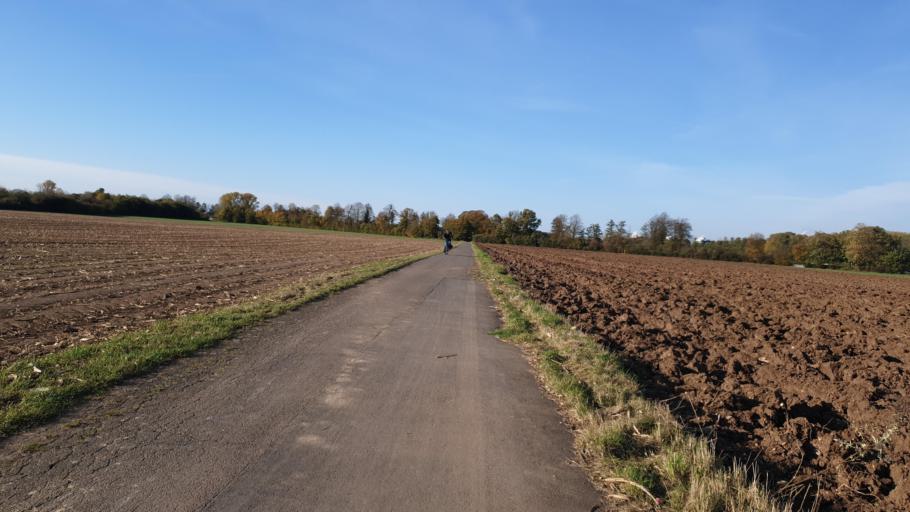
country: DE
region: North Rhine-Westphalia
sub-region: Regierungsbezirk Koln
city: Kerpen
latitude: 50.9208
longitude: 6.6917
